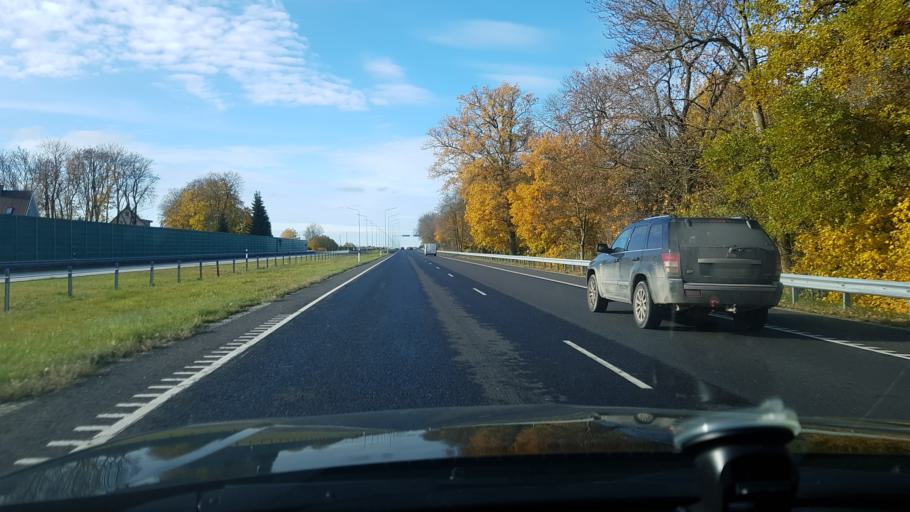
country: EE
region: Harju
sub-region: Kuusalu vald
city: Kuusalu
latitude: 59.4461
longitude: 25.3891
